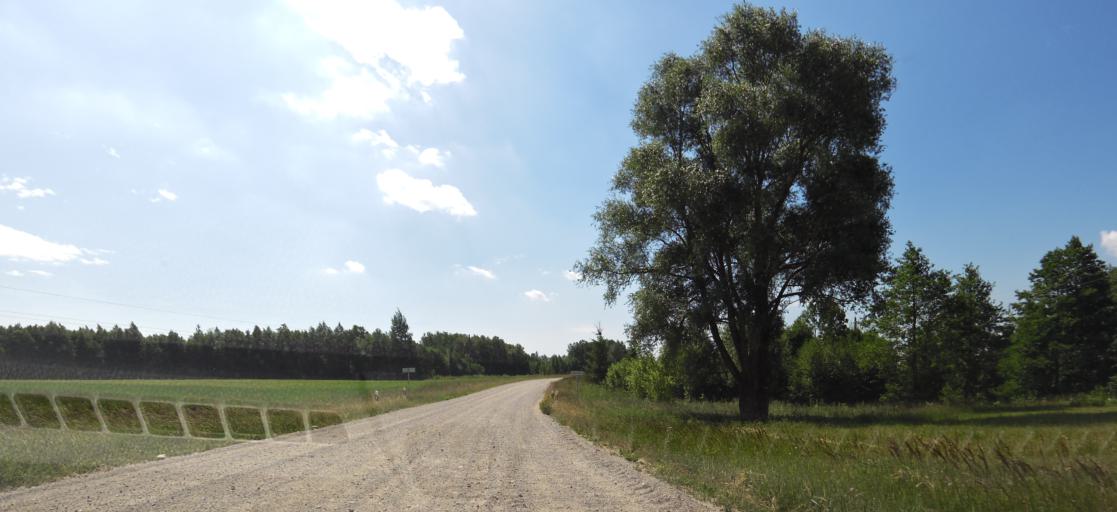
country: LT
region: Panevezys
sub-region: Birzai
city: Birzai
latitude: 56.1871
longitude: 24.9364
